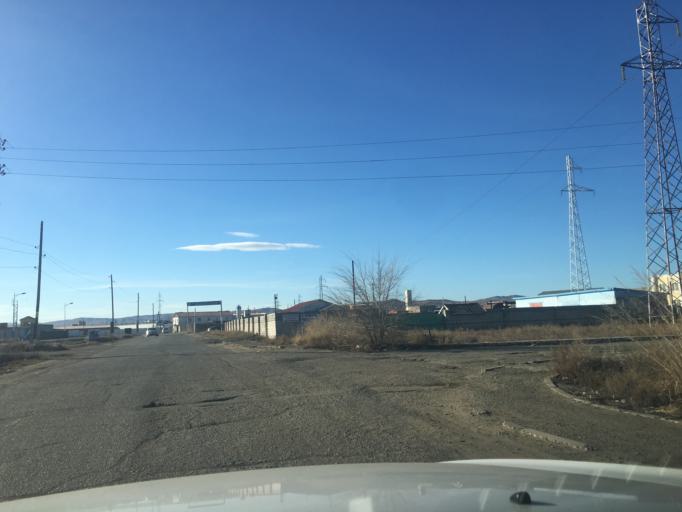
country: MN
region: Ulaanbaatar
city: Ulaanbaatar
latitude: 47.9019
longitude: 106.7780
